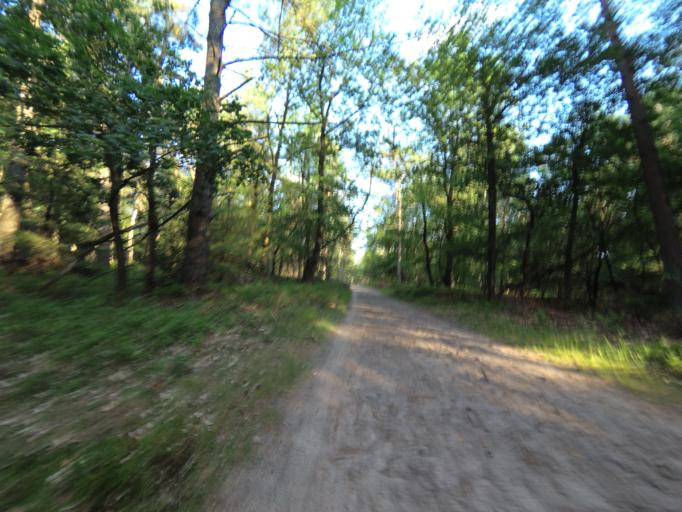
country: NL
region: Gelderland
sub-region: Gemeente Apeldoorn
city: Beekbergen
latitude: 52.1402
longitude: 5.8985
